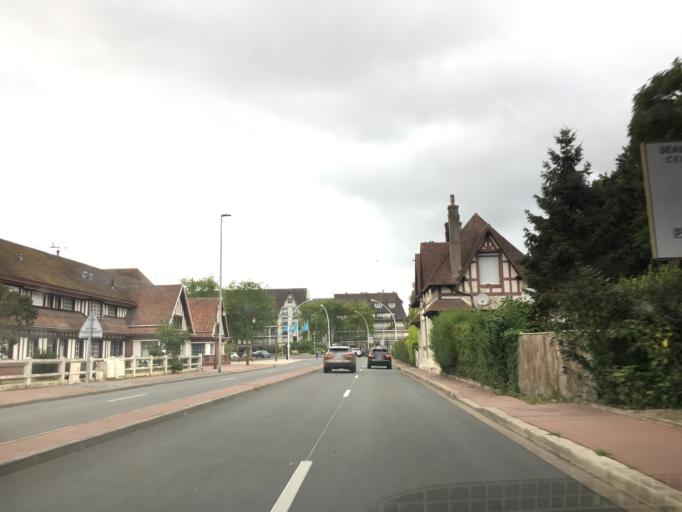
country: FR
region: Lower Normandy
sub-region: Departement du Calvados
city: Trouville-sur-Mer
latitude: 49.3596
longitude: 0.0854
